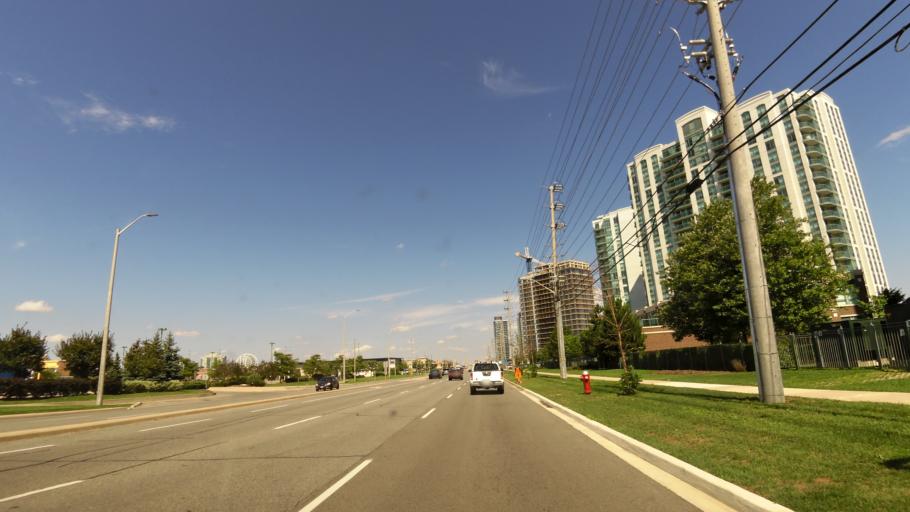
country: CA
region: Ontario
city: Mississauga
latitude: 43.5523
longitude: -79.7139
